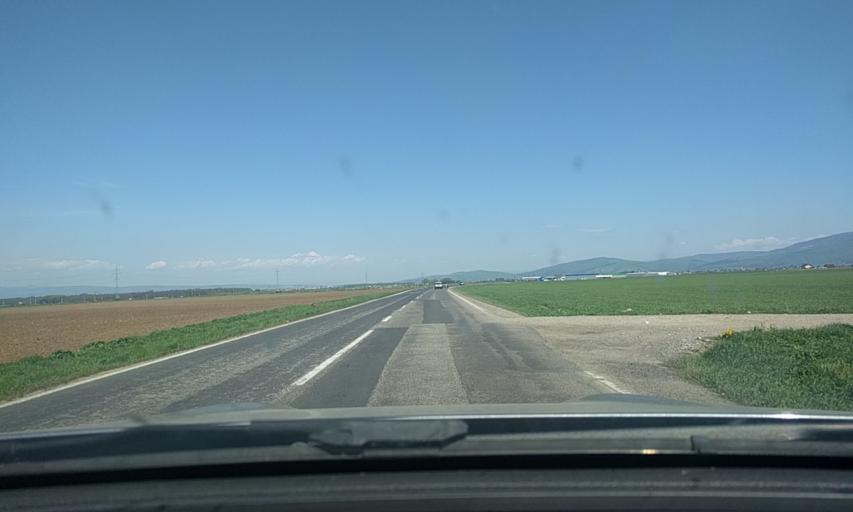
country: RO
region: Brasov
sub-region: Comuna Harman
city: Harman
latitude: 45.7110
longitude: 25.7155
